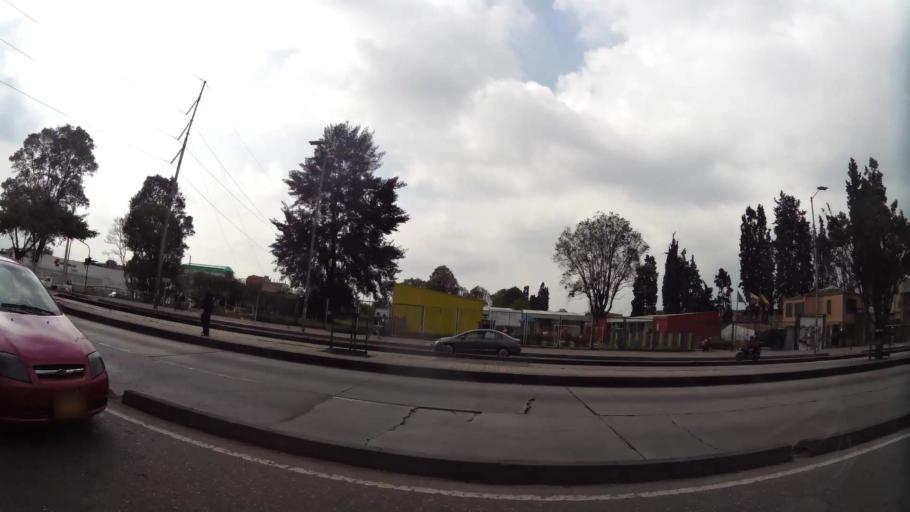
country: CO
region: Bogota D.C.
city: Bogota
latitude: 4.5778
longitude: -74.1103
